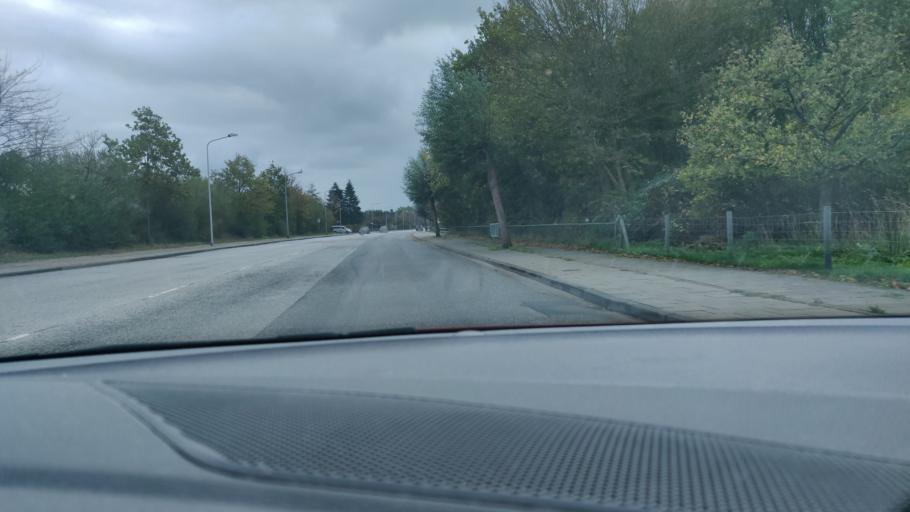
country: DE
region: Lower Saxony
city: Cuxhaven
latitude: 53.8785
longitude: 8.6752
